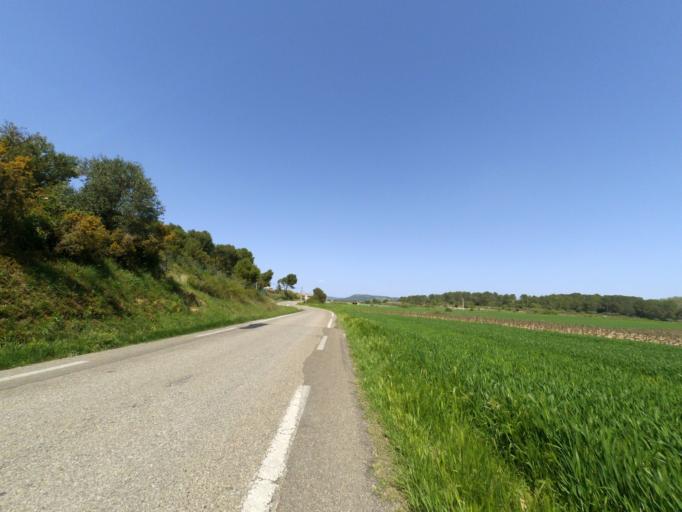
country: FR
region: Languedoc-Roussillon
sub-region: Departement du Gard
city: Mus
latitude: 43.7580
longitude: 4.2001
